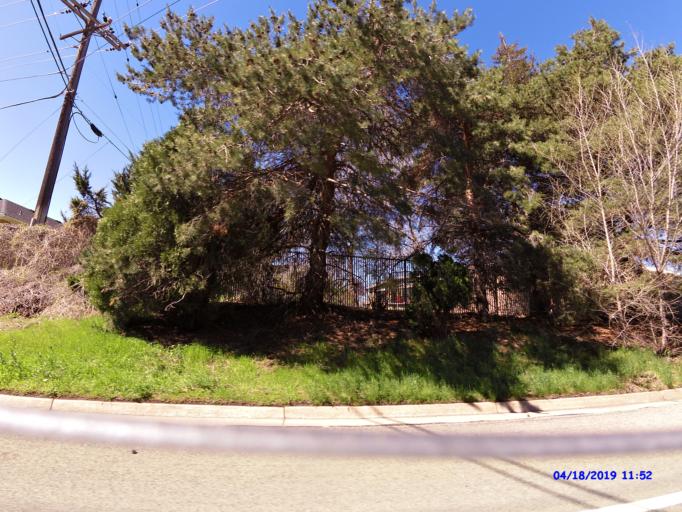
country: US
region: Utah
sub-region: Weber County
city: Ogden
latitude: 41.2466
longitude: -111.9481
